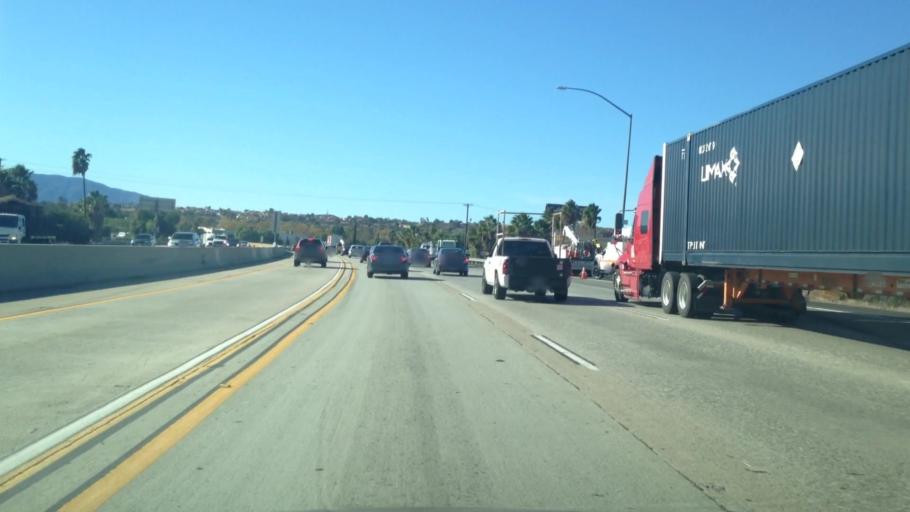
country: US
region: California
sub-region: Riverside County
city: Home Gardens
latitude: 33.8957
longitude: -117.4923
